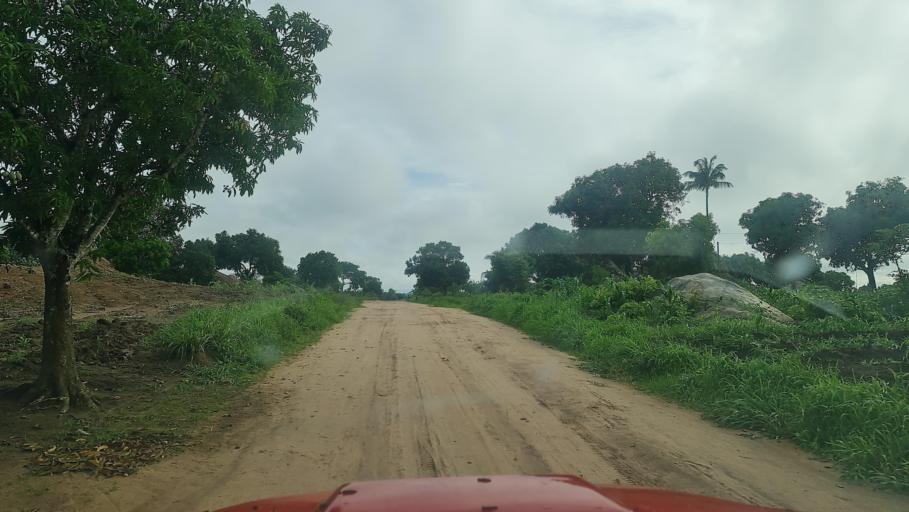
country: MW
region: Southern Region
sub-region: Nsanje District
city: Nsanje
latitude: -17.2892
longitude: 35.6041
